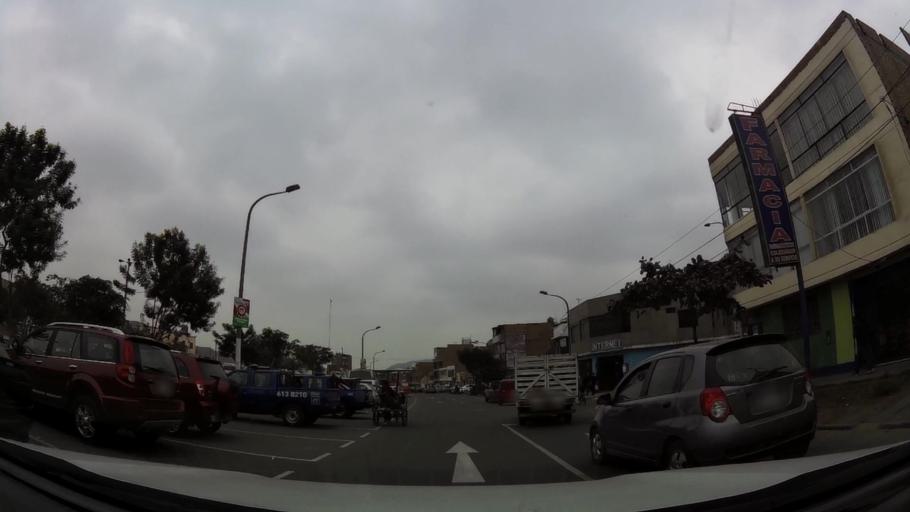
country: PE
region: Lima
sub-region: Lima
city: Independencia
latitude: -11.9340
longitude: -77.0770
